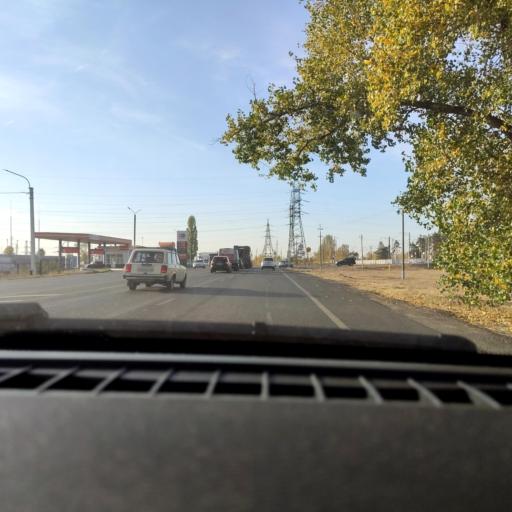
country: RU
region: Voronezj
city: Maslovka
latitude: 51.5919
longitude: 39.2508
